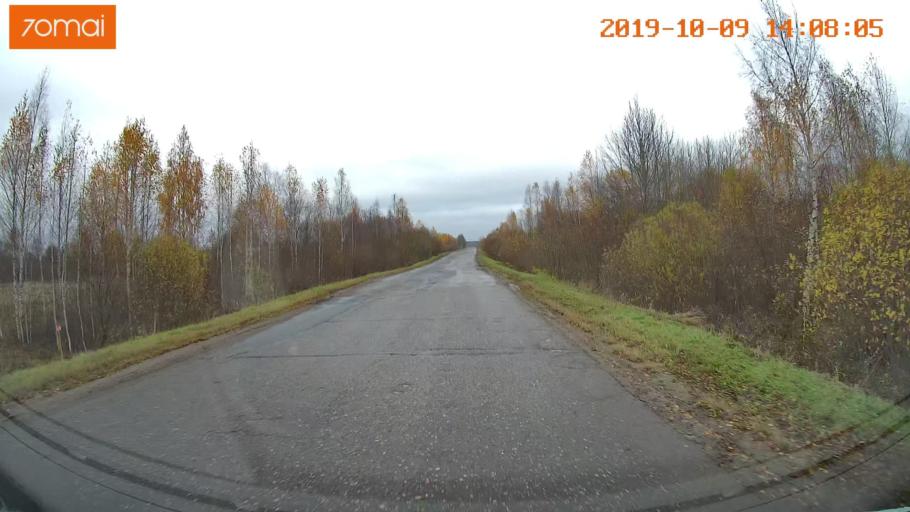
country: RU
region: Kostroma
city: Buy
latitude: 58.4747
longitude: 41.4314
